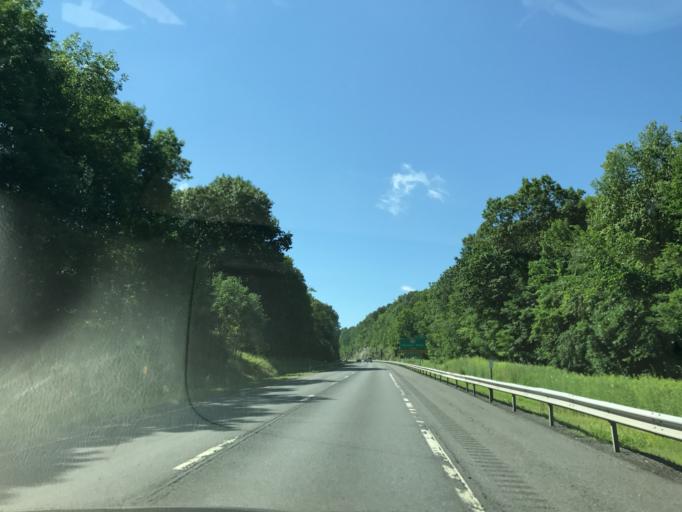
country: US
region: New York
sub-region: Columbia County
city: Chatham
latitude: 42.4339
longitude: -73.5549
